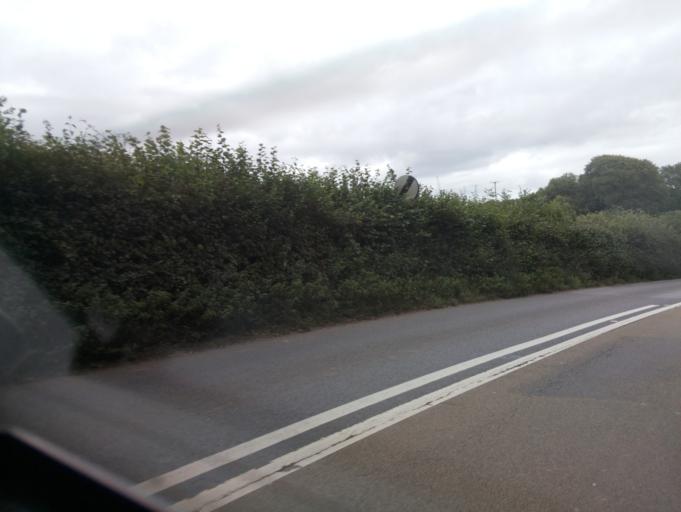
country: GB
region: England
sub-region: Devon
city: Totnes
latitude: 50.4332
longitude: -3.6600
